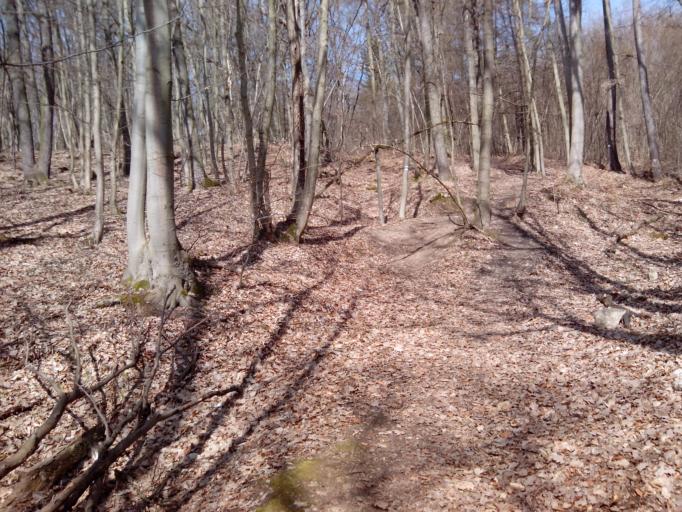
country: CZ
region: Central Bohemia
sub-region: Okres Beroun
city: Beroun
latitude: 49.9331
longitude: 14.1104
